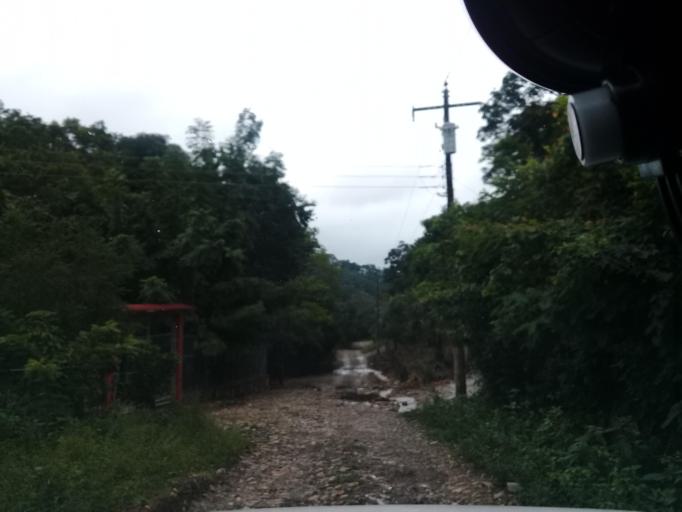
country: MX
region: Veracruz
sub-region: Chalma
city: San Pedro Coyutla
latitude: 21.2372
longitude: -98.4375
